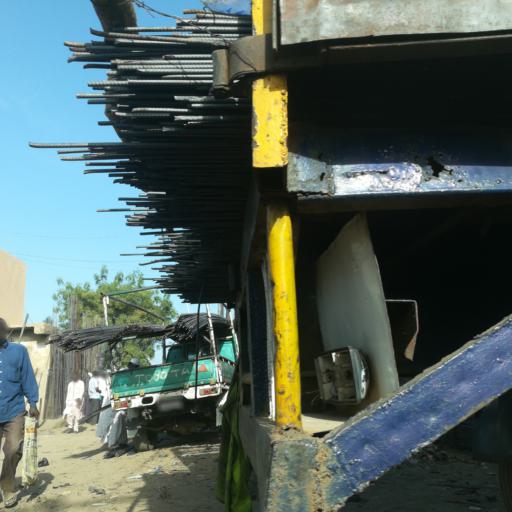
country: NG
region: Kano
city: Kano
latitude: 12.0281
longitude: 8.4998
